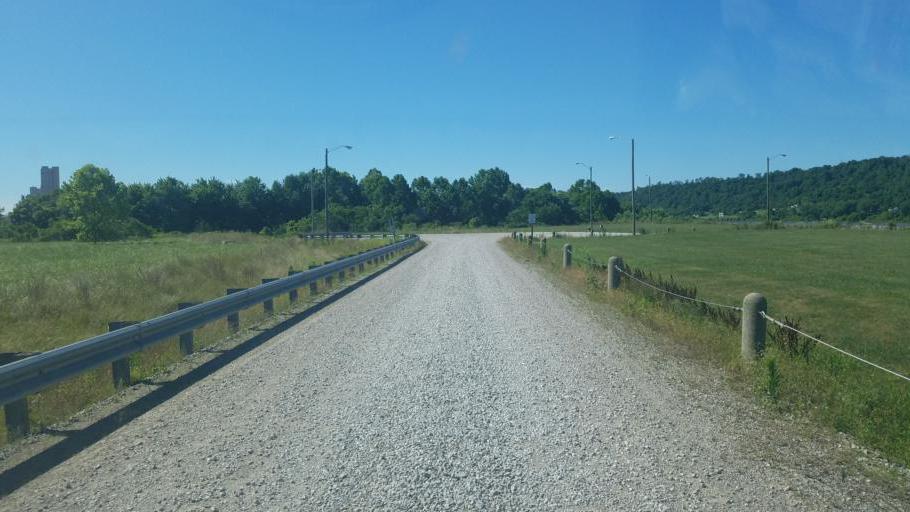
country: US
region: Ohio
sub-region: Gallia County
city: Gallipolis
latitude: 38.6711
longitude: -82.1835
